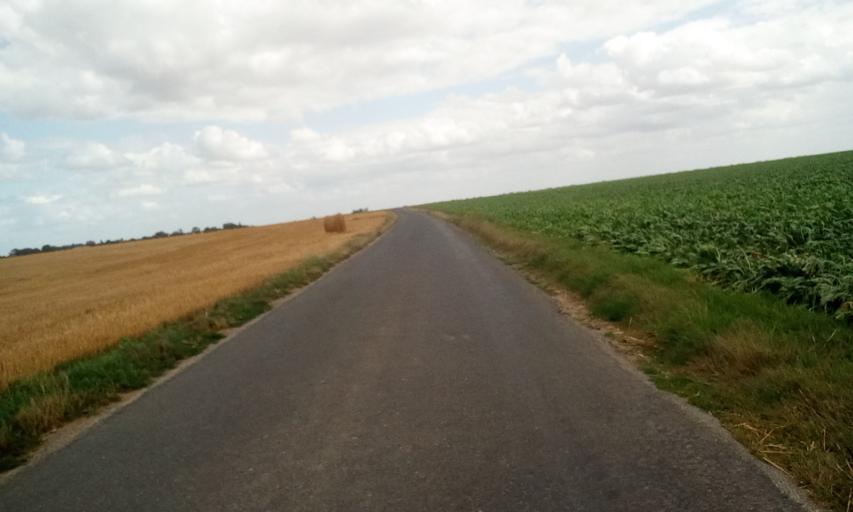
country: FR
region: Lower Normandy
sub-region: Departement du Calvados
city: Ver-sur-Mer
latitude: 49.3139
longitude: -0.5388
